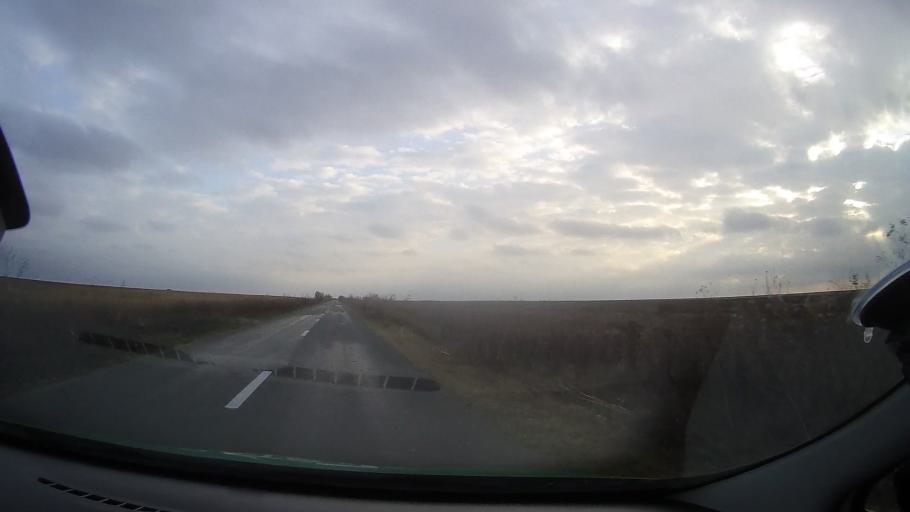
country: RO
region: Constanta
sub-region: Comuna Pestera
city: Pestera
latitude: 44.1396
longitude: 28.1174
